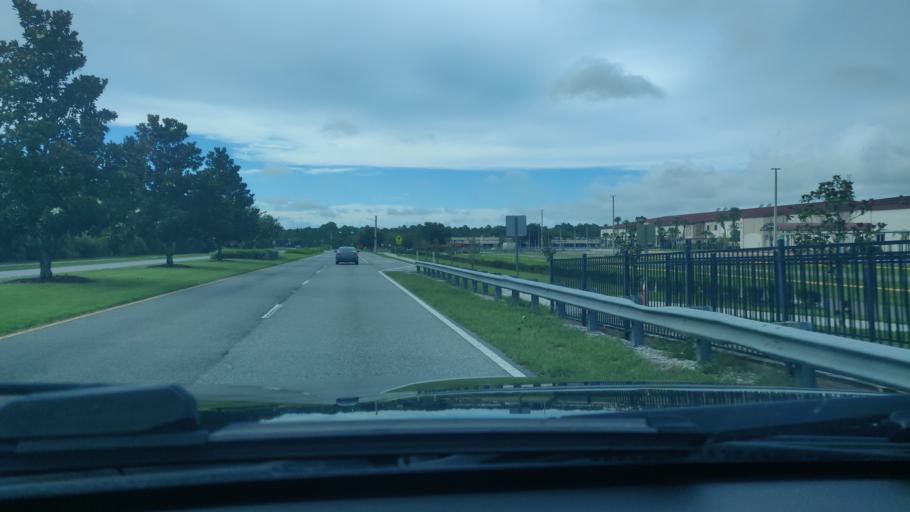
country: US
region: Florida
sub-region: Flagler County
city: Palm Coast
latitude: 29.5286
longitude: -81.2254
